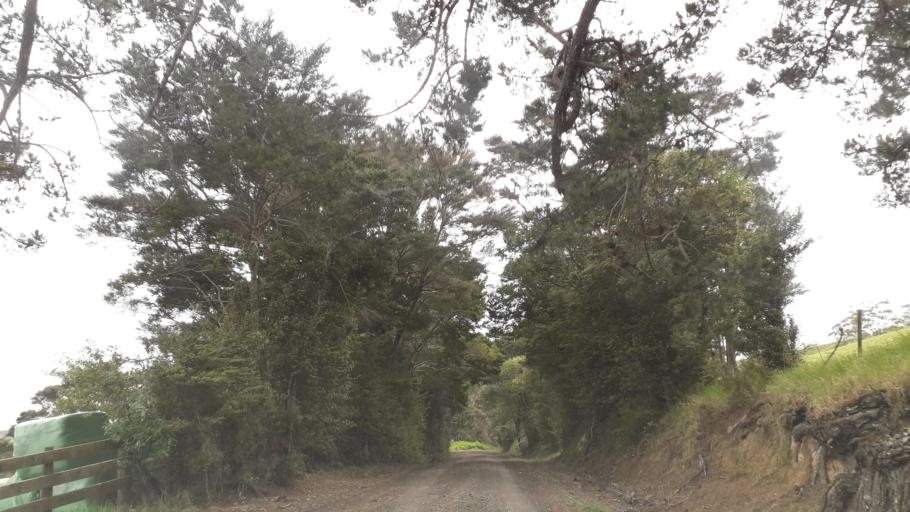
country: NZ
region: Northland
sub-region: Far North District
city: Waimate North
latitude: -35.3176
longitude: 173.5741
